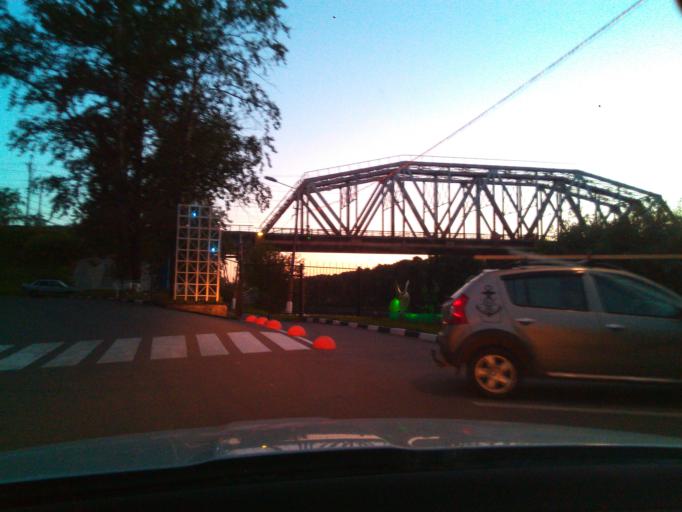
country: RU
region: Moskovskaya
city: Dolgoprudnyy
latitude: 55.9629
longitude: 37.5094
